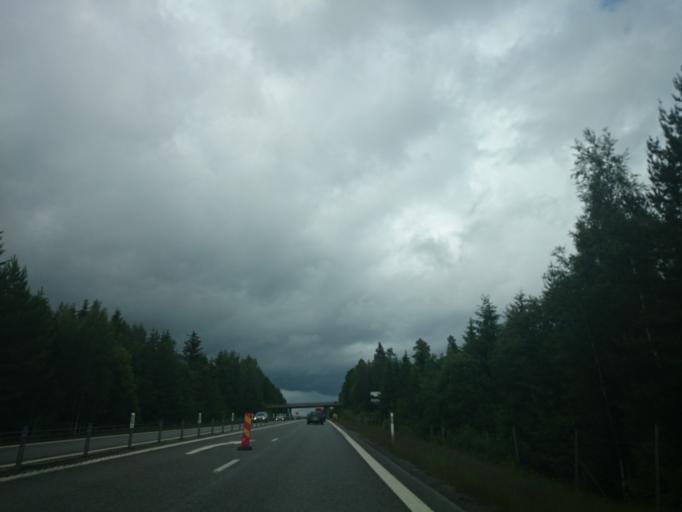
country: SE
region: Vaesternorrland
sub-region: Sundsvalls Kommun
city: Njurundabommen
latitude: 62.2552
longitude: 17.3715
